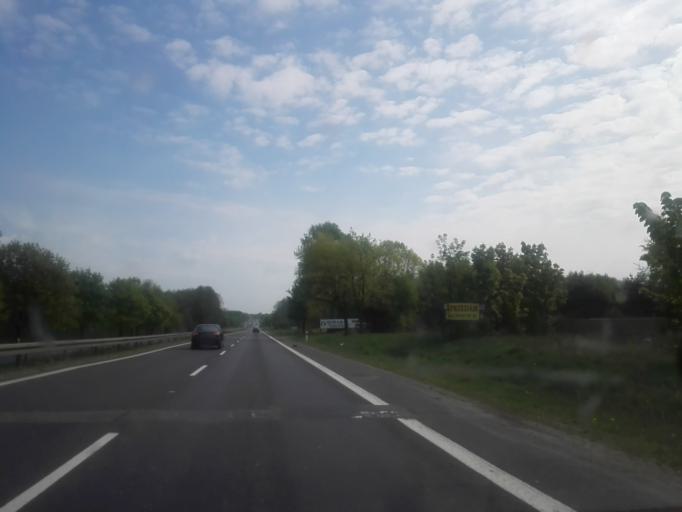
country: PL
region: Masovian Voivodeship
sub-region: Powiat zyrardowski
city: Radziejowice
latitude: 52.0139
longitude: 20.6186
